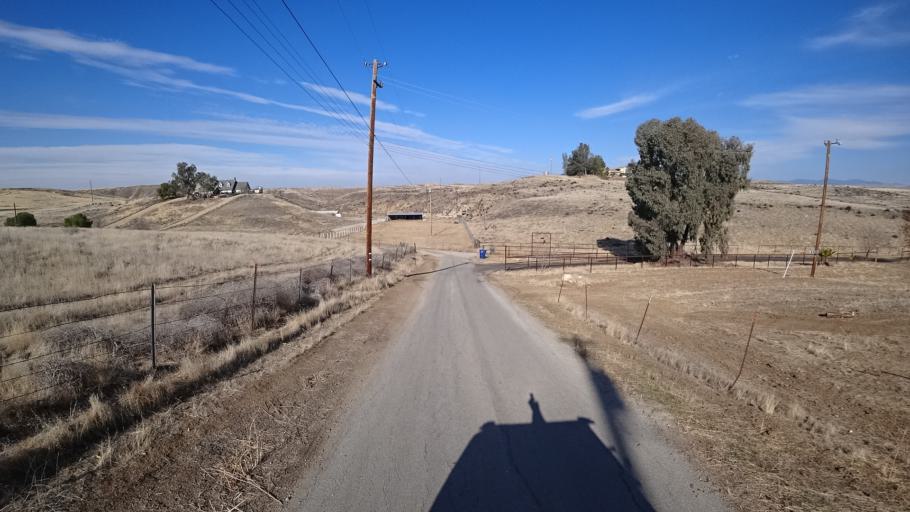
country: US
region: California
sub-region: Kern County
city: Oildale
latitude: 35.4178
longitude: -118.8987
